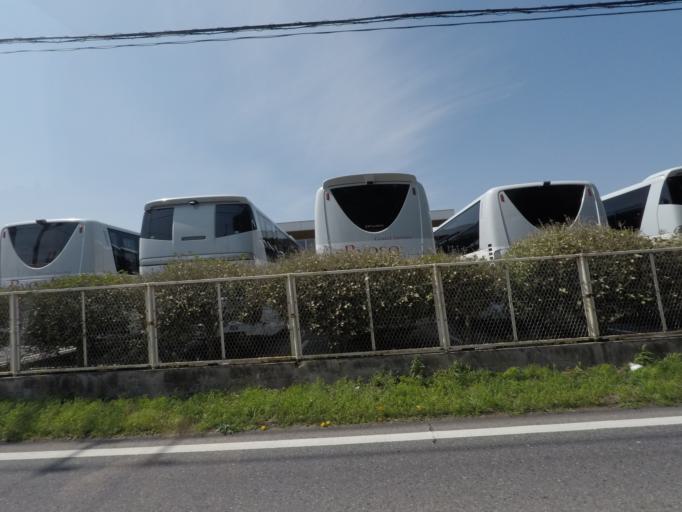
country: JP
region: Chiba
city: Narita
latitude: 35.7723
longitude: 140.3528
